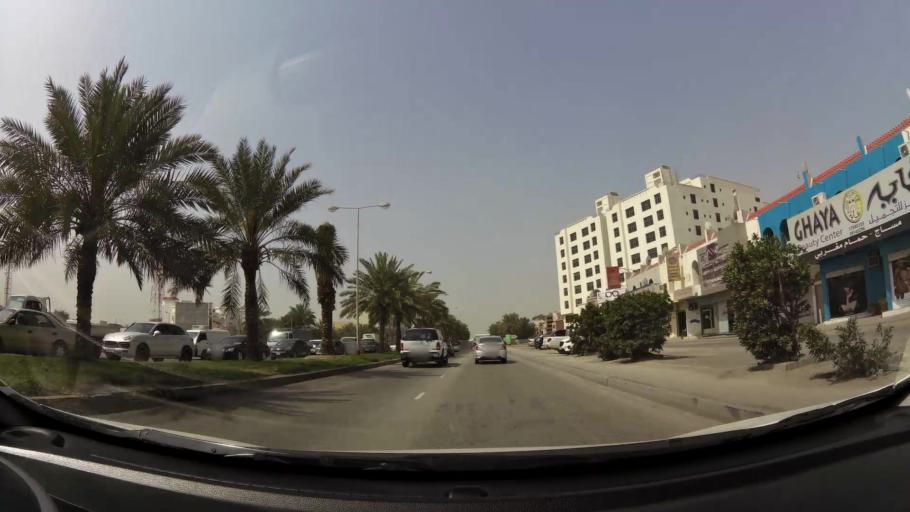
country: BH
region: Manama
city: Jidd Hafs
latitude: 26.2206
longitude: 50.5046
